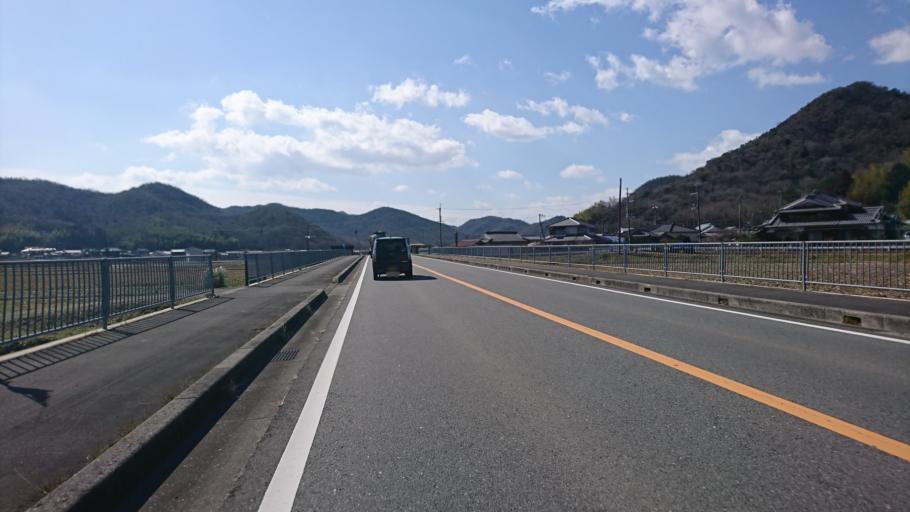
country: JP
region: Hyogo
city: Kakogawacho-honmachi
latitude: 34.8631
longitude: 134.7914
